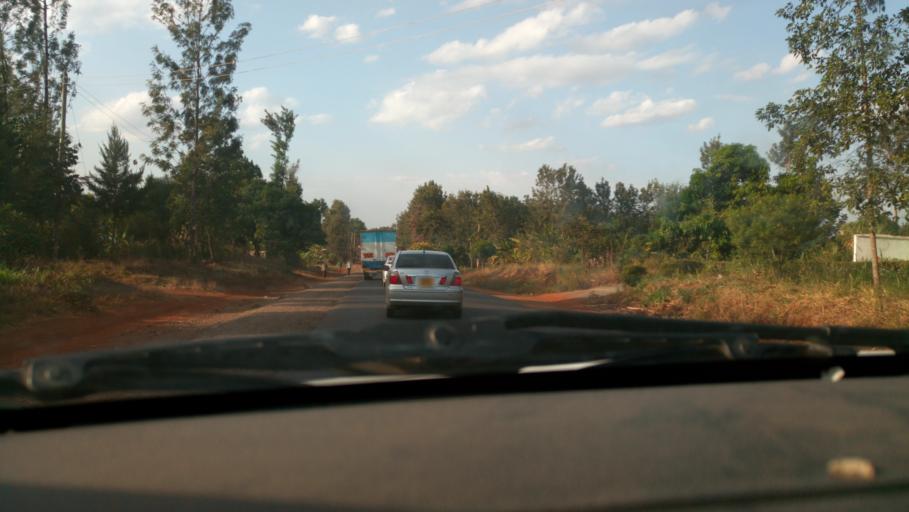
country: KE
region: Murang'a District
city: Maragua
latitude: -0.8147
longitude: 37.1404
